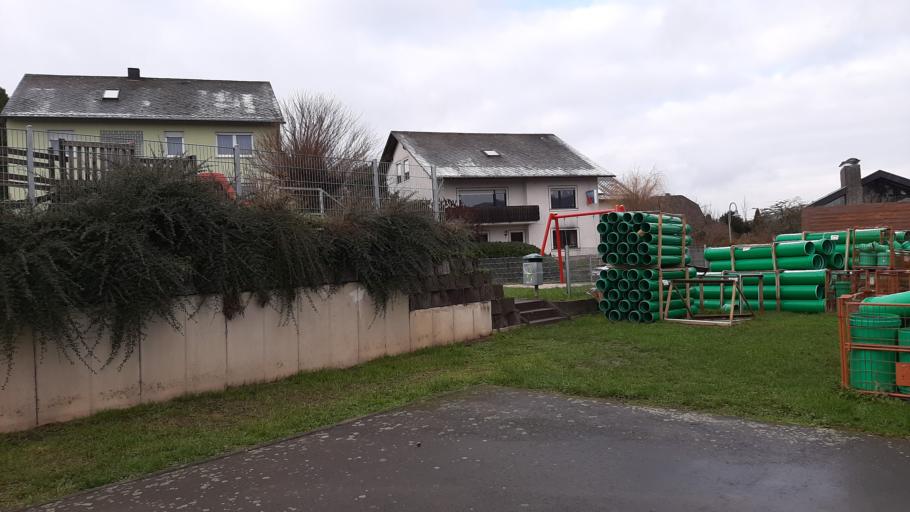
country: DE
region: Rheinland-Pfalz
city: Zell
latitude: 50.0285
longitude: 7.1690
